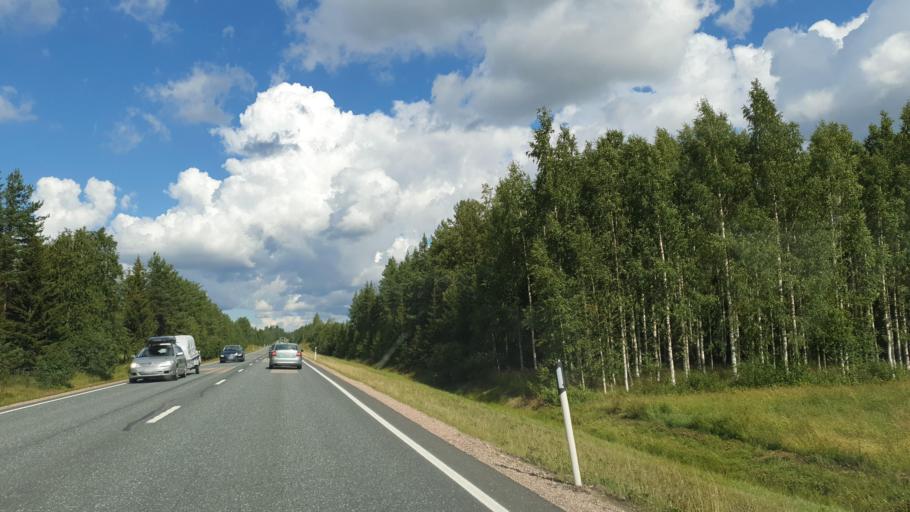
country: FI
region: Kainuu
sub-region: Kajaani
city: Kajaani
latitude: 64.0412
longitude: 27.4494
